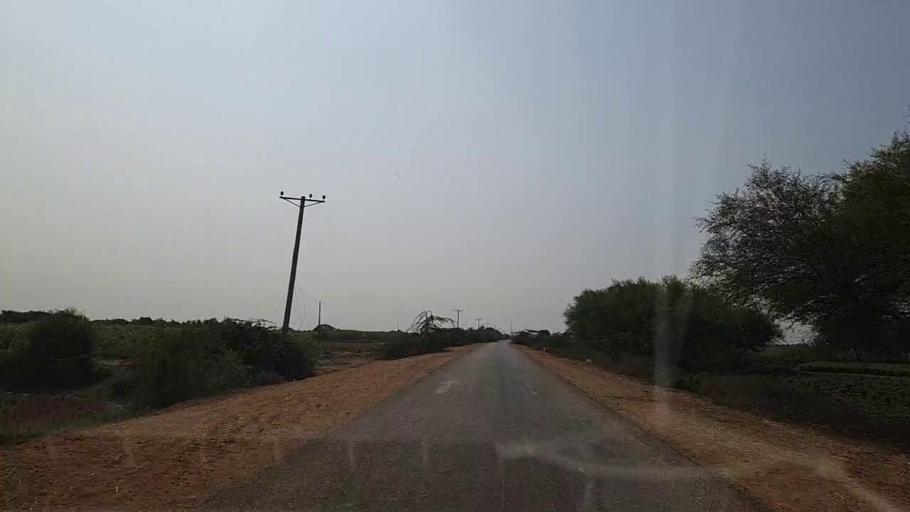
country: PK
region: Sindh
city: Chuhar Jamali
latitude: 24.3004
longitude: 67.9327
